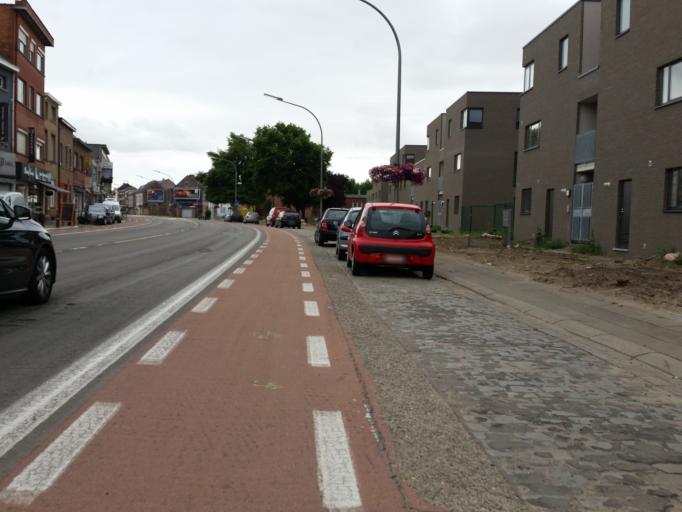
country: BE
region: Flanders
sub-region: Provincie Antwerpen
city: Mechelen
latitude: 51.0432
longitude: 4.4772
